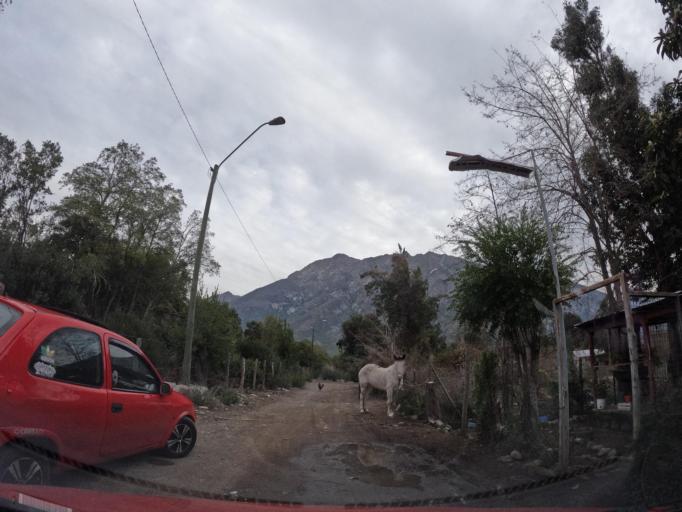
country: CL
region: Maule
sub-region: Provincia de Linares
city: Colbun
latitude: -35.7236
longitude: -71.0177
